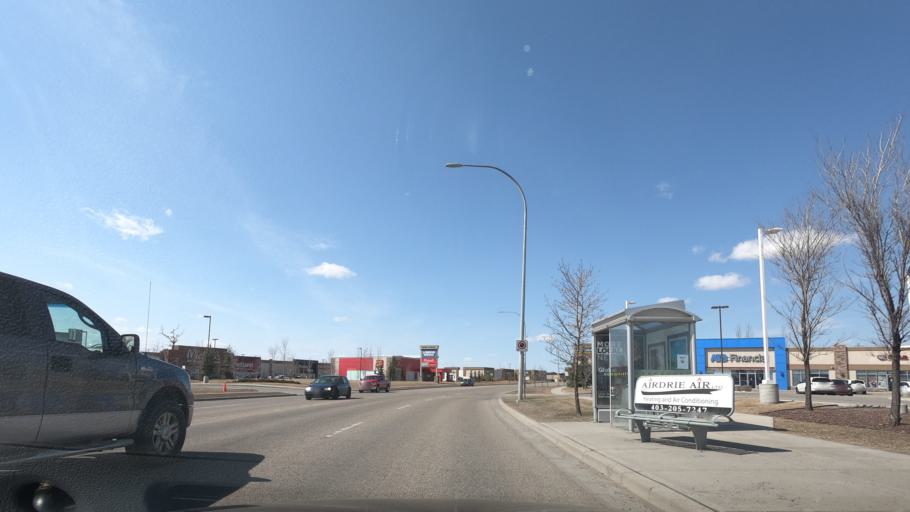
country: CA
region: Alberta
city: Airdrie
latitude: 51.2645
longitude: -114.0054
